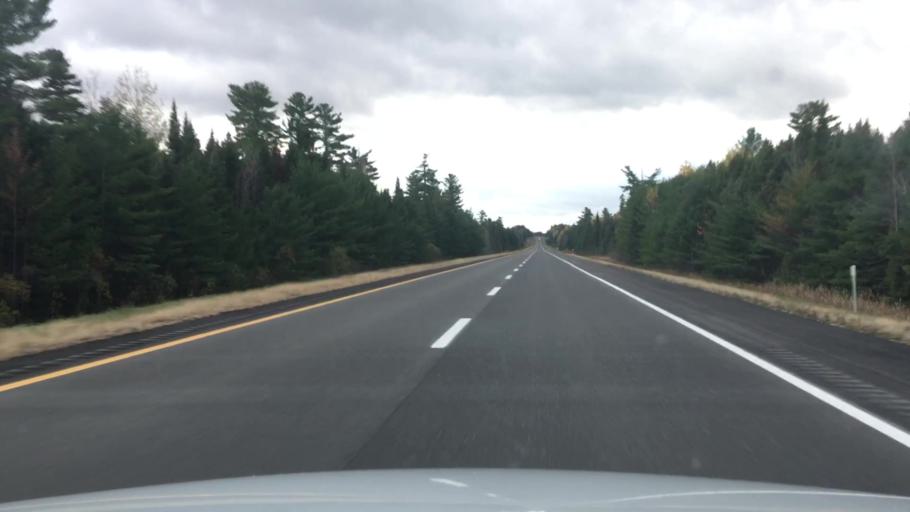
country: US
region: Maine
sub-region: Penobscot County
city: Patten
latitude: 46.0735
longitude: -68.2212
